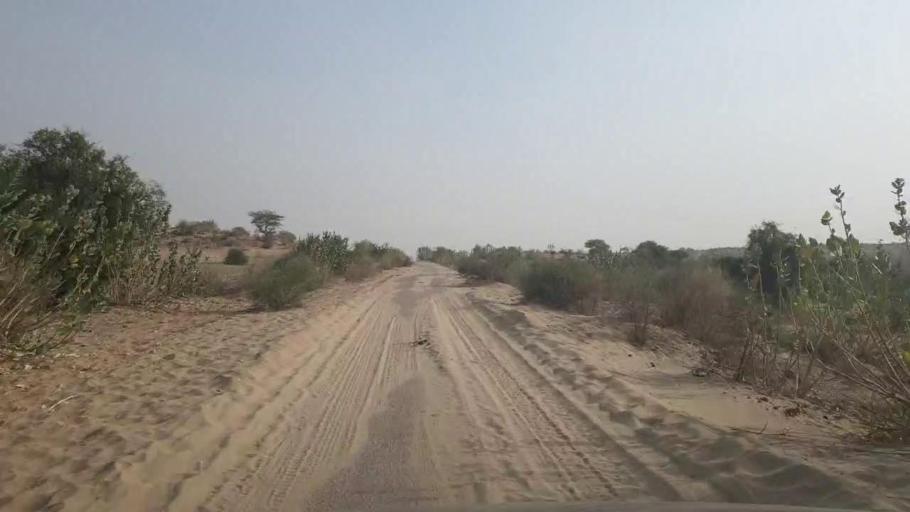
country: PK
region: Sindh
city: Chor
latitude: 25.5145
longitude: 69.9656
